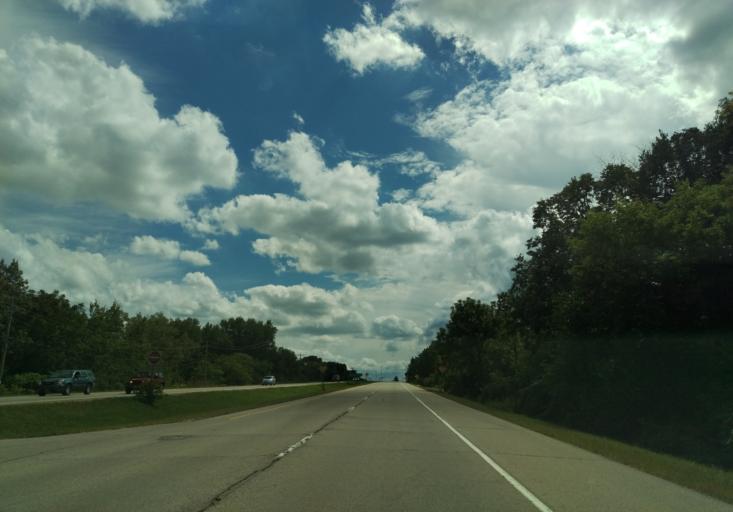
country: US
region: Wisconsin
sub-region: Dane County
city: Maple Bluff
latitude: 43.1450
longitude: -89.3958
